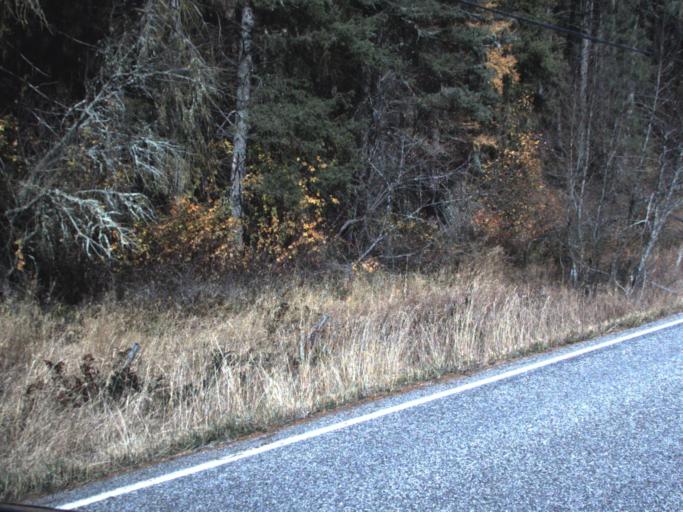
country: CA
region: British Columbia
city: Grand Forks
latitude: 48.9483
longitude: -118.5506
